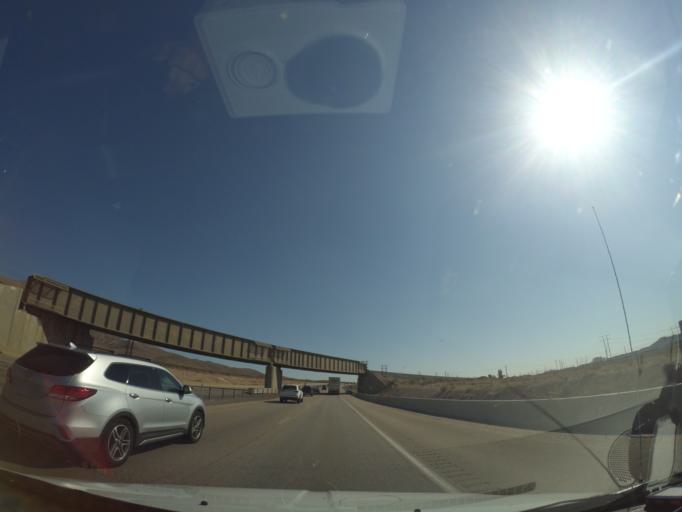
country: US
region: Nevada
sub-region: Clark County
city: Nellis Air Force Base
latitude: 36.3600
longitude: -114.9033
